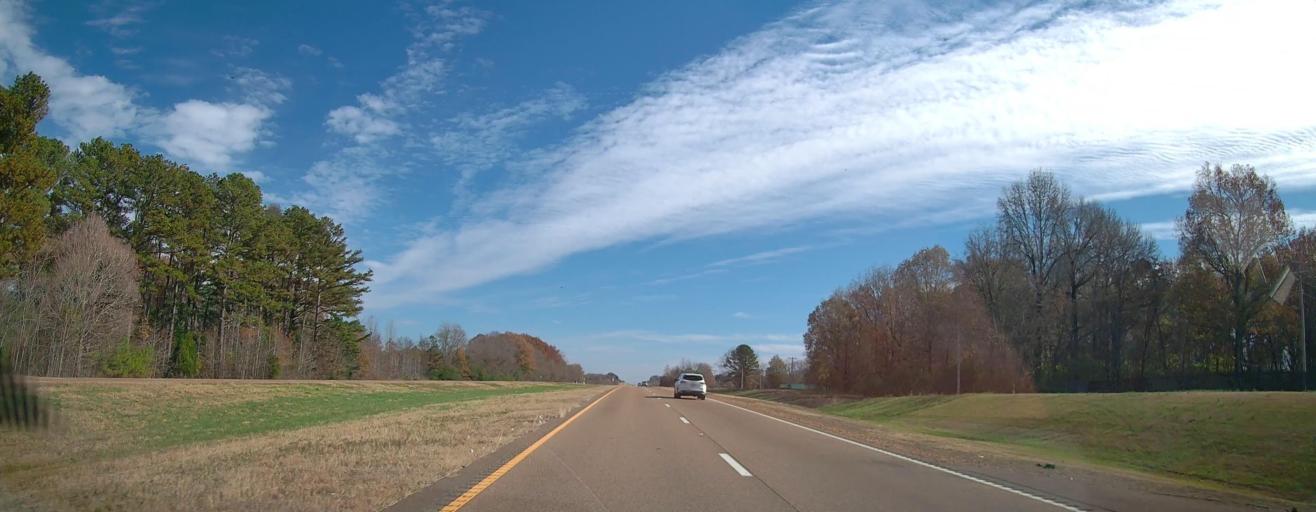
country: US
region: Mississippi
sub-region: Benton County
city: Ashland
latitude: 34.9463
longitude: -89.2862
